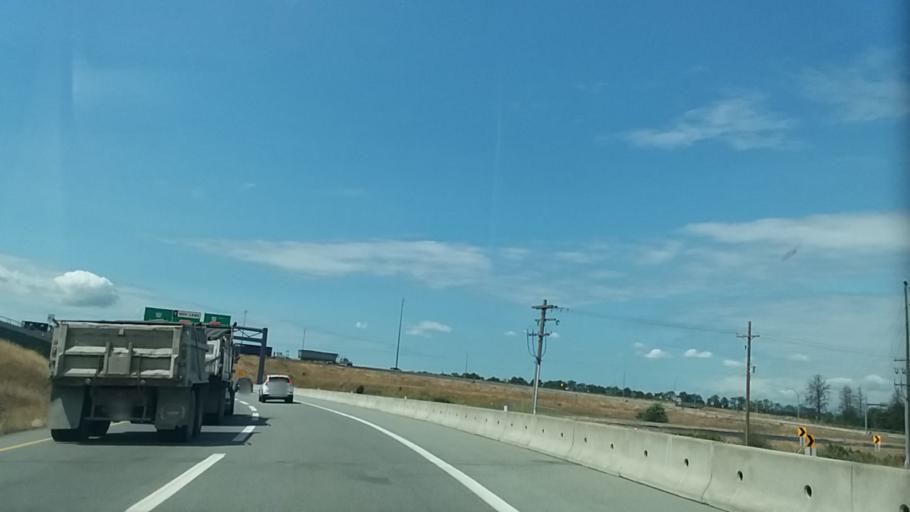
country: CA
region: British Columbia
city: Ladner
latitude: 49.0956
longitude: -123.0233
